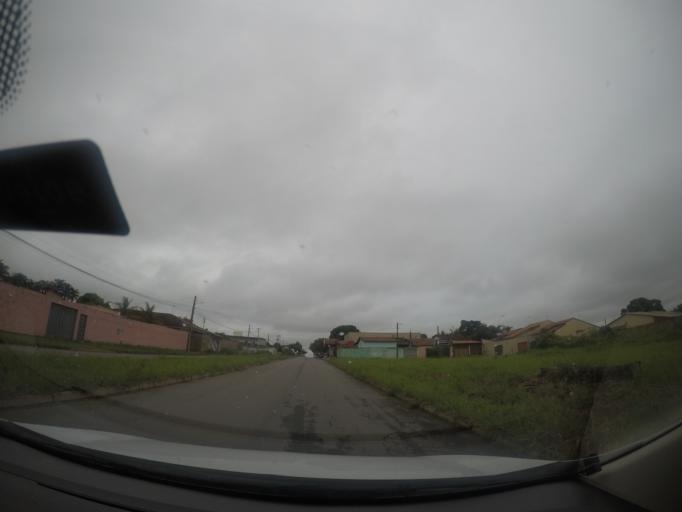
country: BR
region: Goias
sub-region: Goiania
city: Goiania
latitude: -16.7535
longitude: -49.3175
